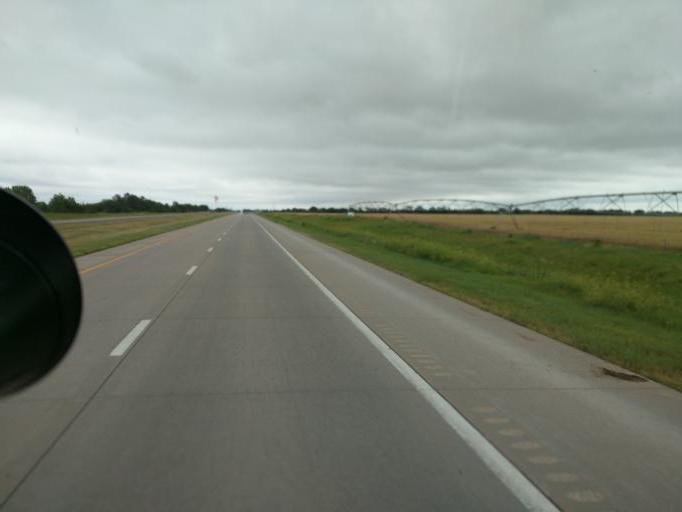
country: US
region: Kansas
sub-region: Reno County
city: South Hutchinson
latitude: 37.9537
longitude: -97.8998
